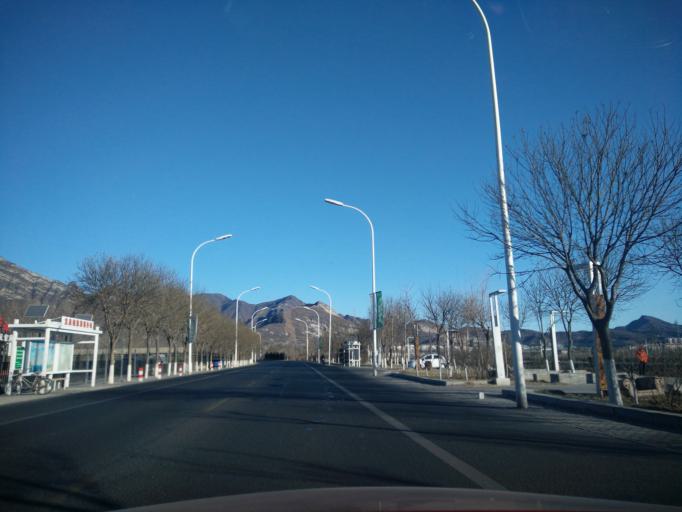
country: CN
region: Beijing
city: Junzhuang
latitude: 39.9881
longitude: 116.0807
